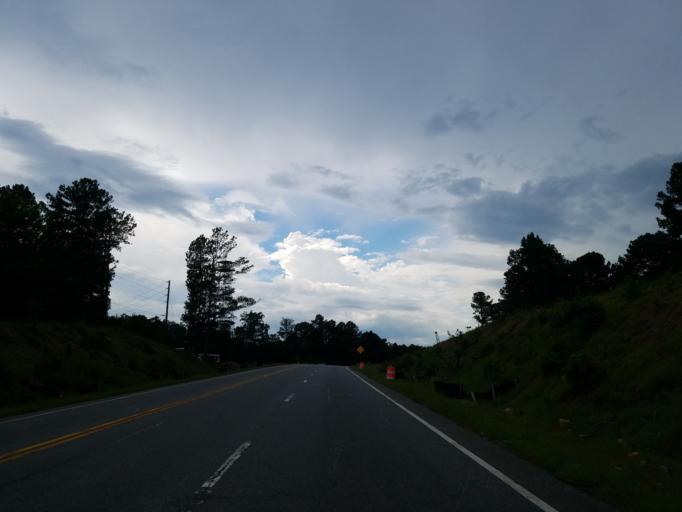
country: US
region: Georgia
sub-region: Bartow County
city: Adairsville
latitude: 34.3162
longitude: -84.8964
